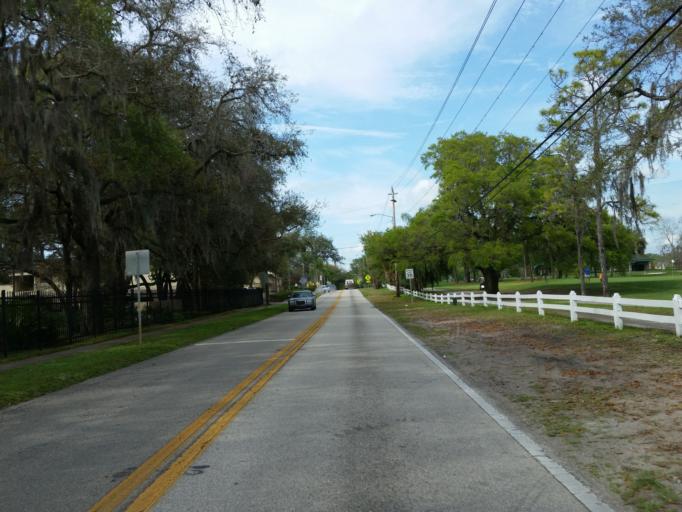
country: US
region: Florida
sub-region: Hillsborough County
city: University
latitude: 28.0750
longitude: -82.4100
